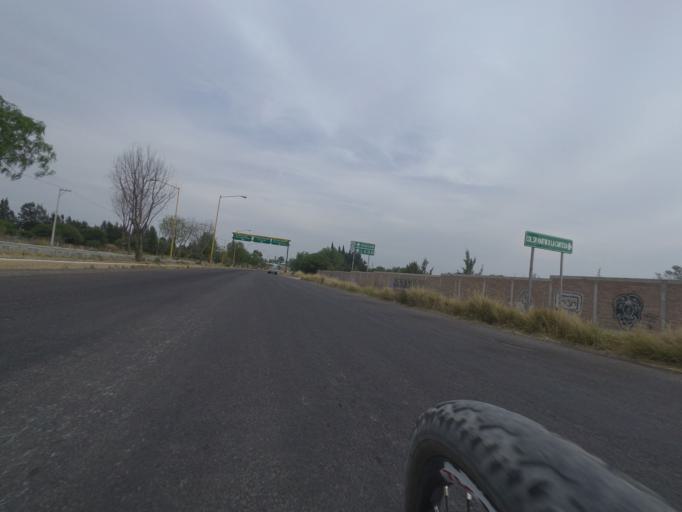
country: MX
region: Aguascalientes
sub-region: Aguascalientes
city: La Loma de los Negritos
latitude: 21.8559
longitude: -102.3569
